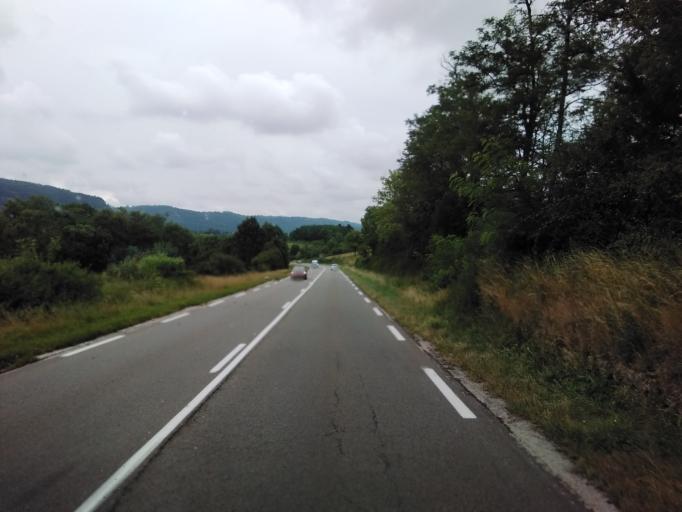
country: FR
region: Franche-Comte
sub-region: Departement du Jura
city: Poligny
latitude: 46.8612
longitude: 5.7132
